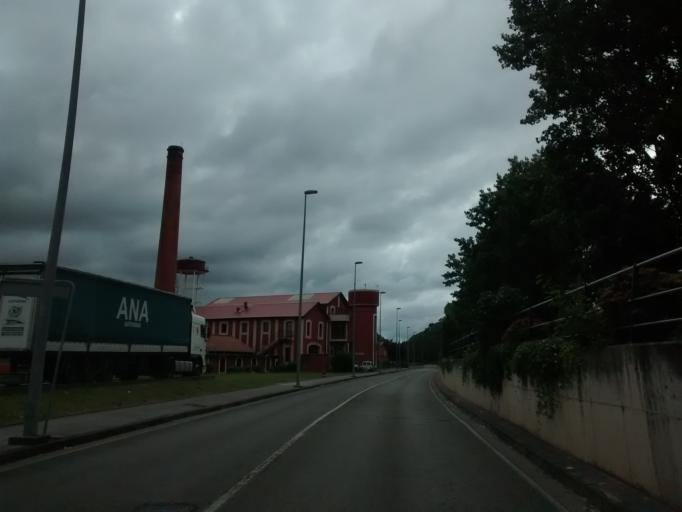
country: ES
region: Cantabria
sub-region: Provincia de Cantabria
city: Torrelavega
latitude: 43.3557
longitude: -4.0541
